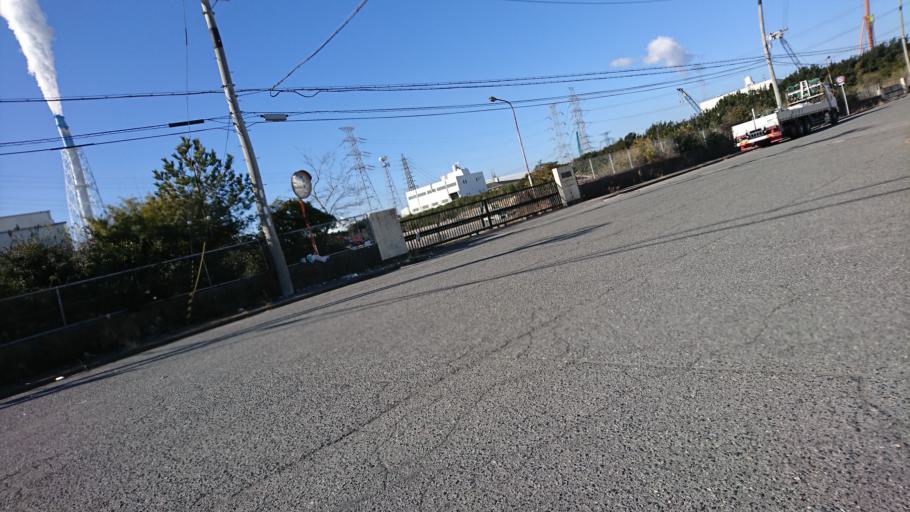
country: JP
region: Hyogo
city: Shirahamacho-usazakiminami
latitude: 34.7574
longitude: 134.7701
